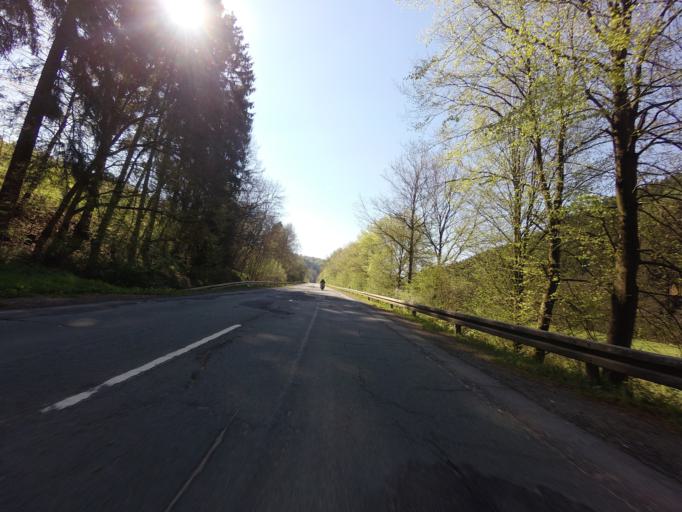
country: DE
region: North Rhine-Westphalia
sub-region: Regierungsbezirk Arnsberg
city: Drolshagen
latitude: 51.0891
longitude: 7.7537
